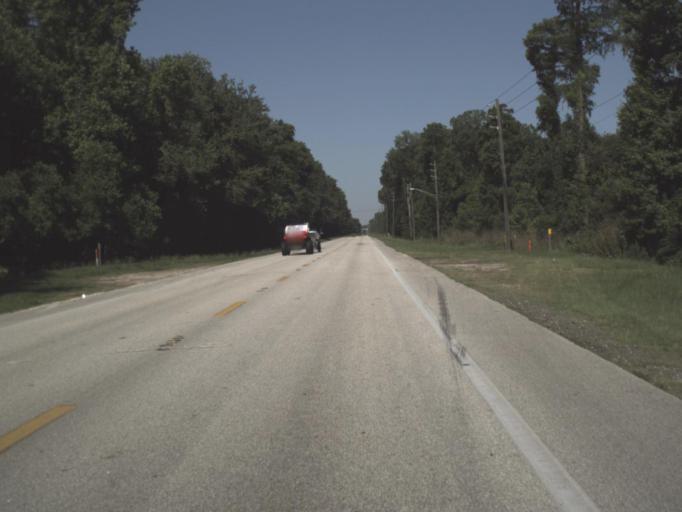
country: US
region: Florida
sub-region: Duval County
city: Baldwin
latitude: 30.3071
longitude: -81.9165
